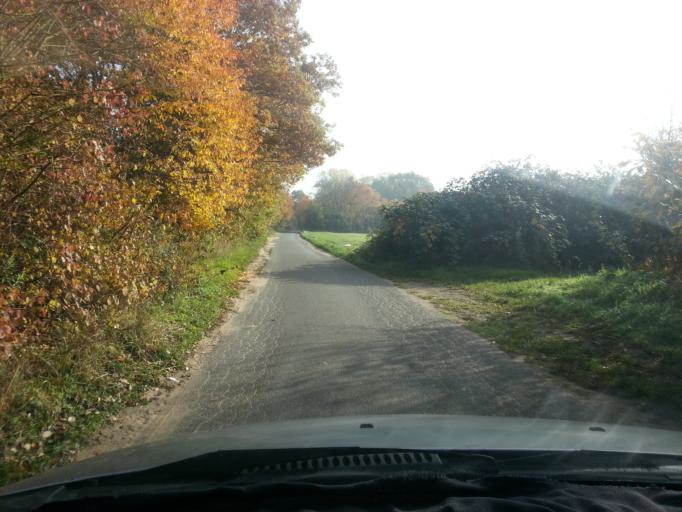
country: DE
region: Hesse
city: Dreieich
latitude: 50.0095
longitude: 8.6803
